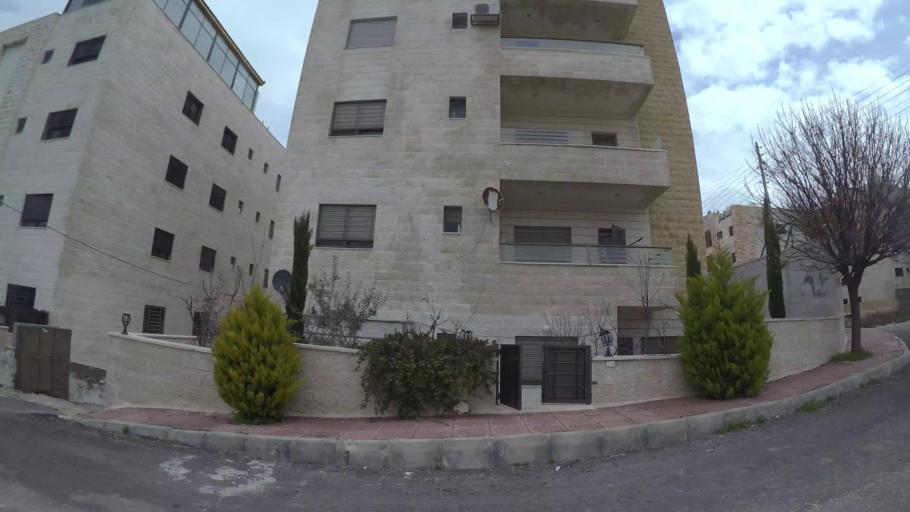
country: JO
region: Amman
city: Umm as Summaq
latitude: 31.9067
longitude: 35.8391
